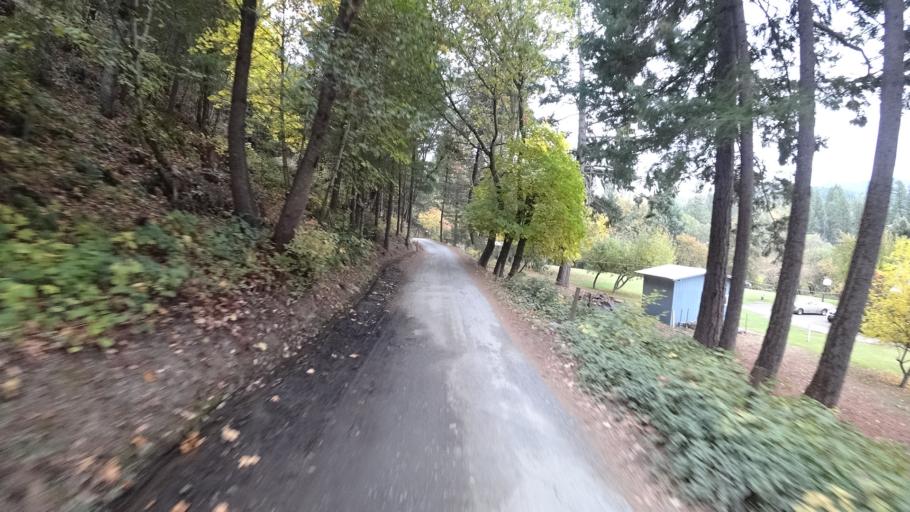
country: US
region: California
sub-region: Siskiyou County
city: Happy Camp
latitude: 41.8013
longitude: -123.3828
